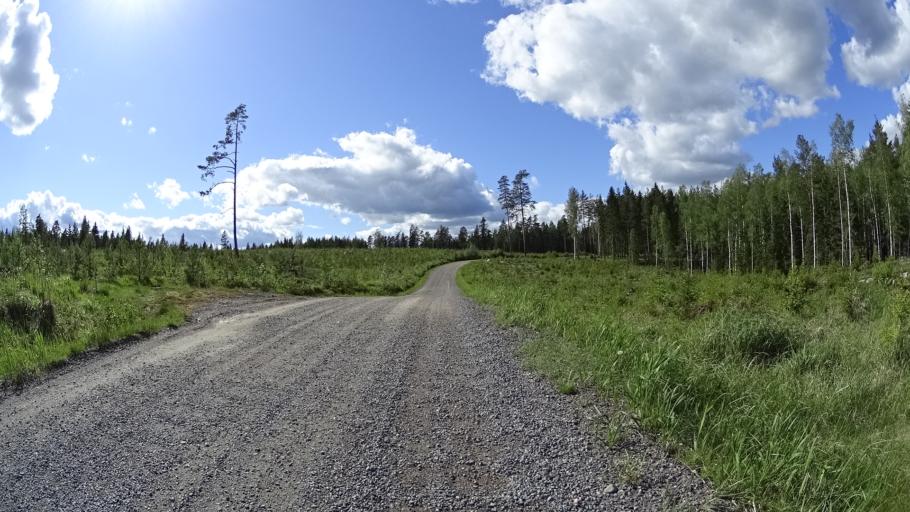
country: FI
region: Varsinais-Suomi
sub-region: Salo
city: Kisko
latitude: 60.1902
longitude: 23.5590
